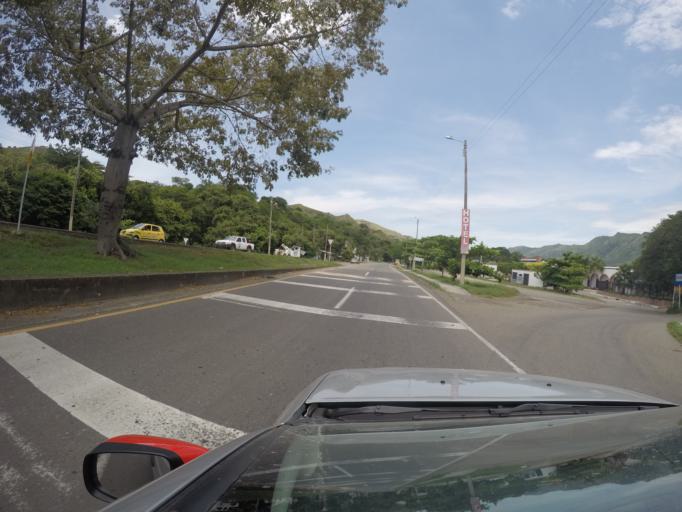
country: CO
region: Tolima
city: Honda
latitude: 5.2127
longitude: -74.7382
